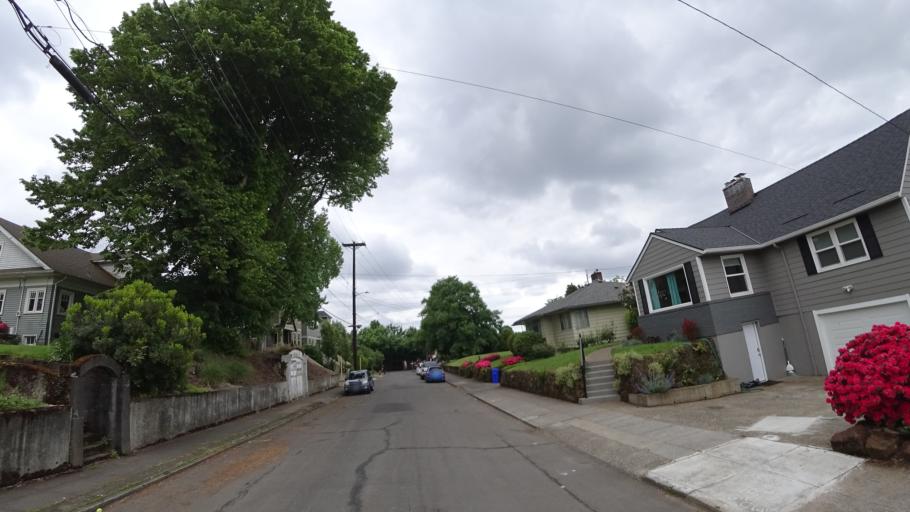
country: US
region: Oregon
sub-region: Multnomah County
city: Lents
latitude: 45.5200
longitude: -122.6103
